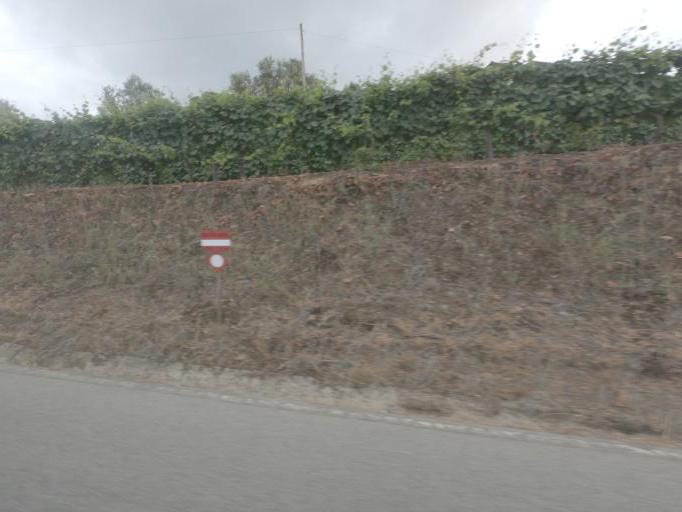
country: PT
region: Vila Real
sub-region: Sabrosa
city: Sabrosa
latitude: 41.2829
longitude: -7.5427
